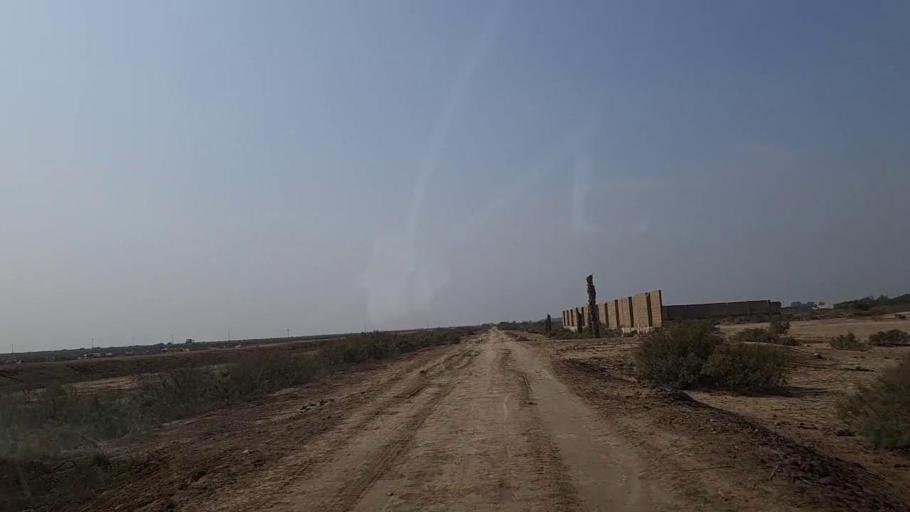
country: PK
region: Sindh
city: Gharo
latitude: 24.6735
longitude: 67.7103
